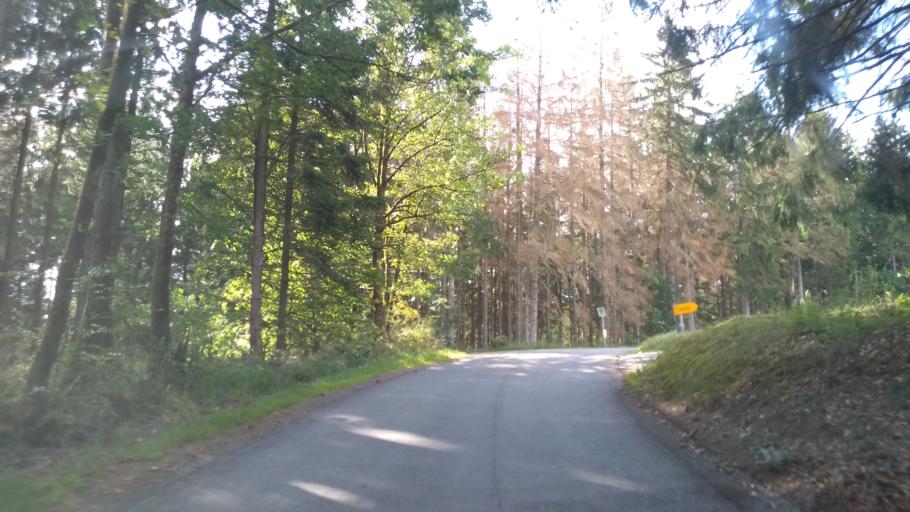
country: DE
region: North Rhine-Westphalia
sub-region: Regierungsbezirk Arnsberg
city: Schalksmuhle
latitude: 51.2126
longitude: 7.5489
